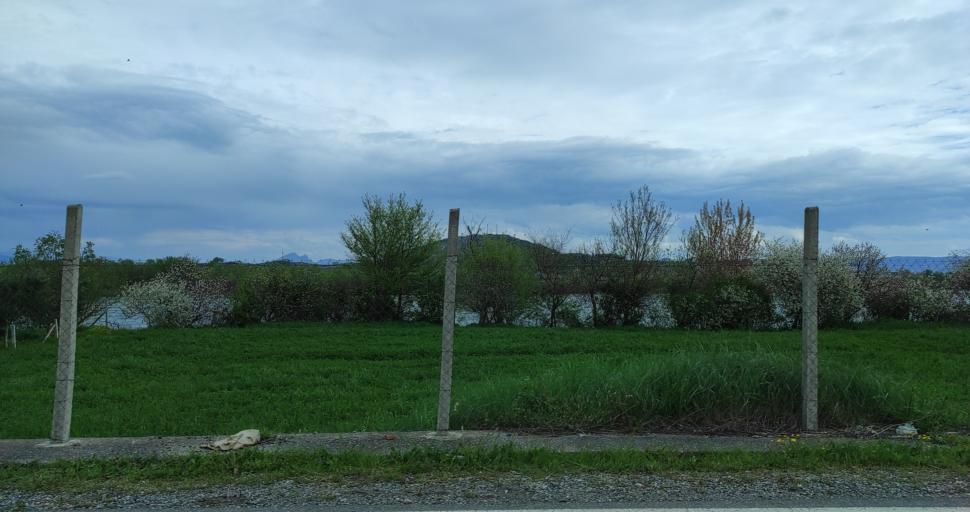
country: AL
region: Shkoder
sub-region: Rrethi i Shkodres
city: Berdica e Madhe
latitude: 42.0317
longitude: 19.4751
